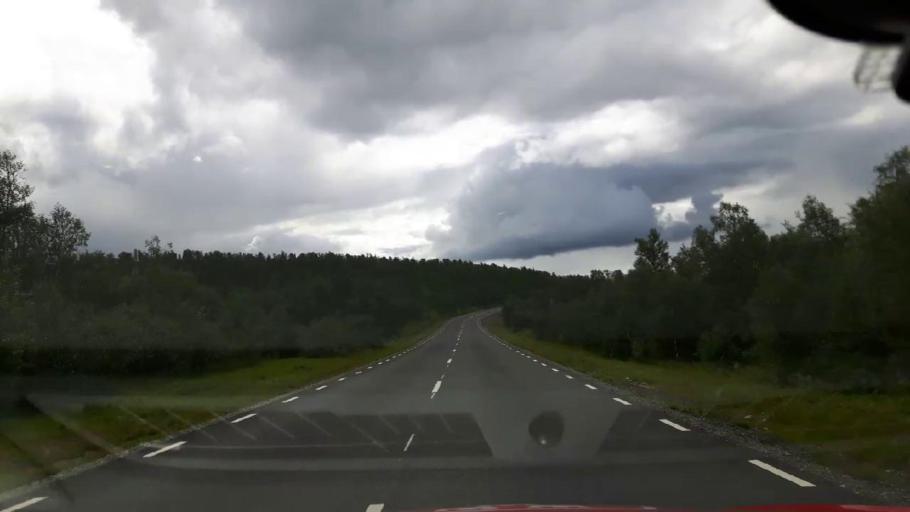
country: NO
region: Nord-Trondelag
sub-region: Royrvik
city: Royrvik
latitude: 64.9764
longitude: 14.2129
